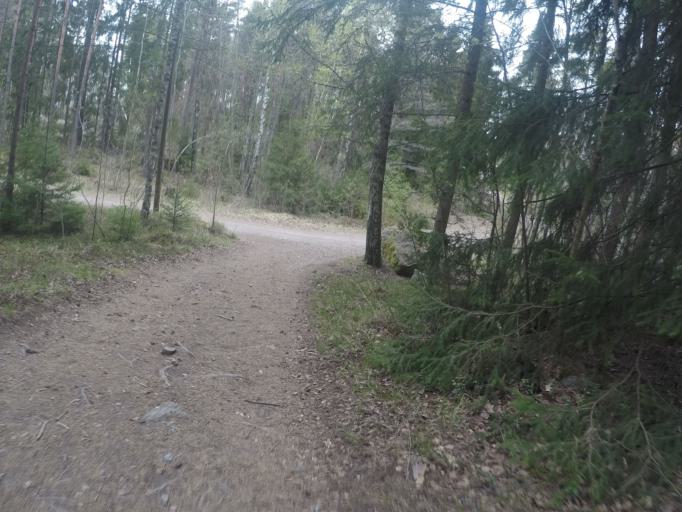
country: SE
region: Vaestmanland
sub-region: Vasteras
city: Vasteras
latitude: 59.6301
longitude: 16.5239
